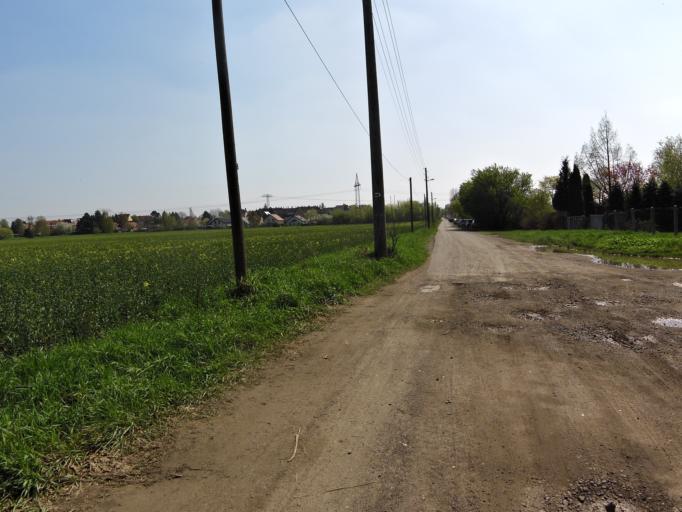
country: DE
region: Saxony
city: Rackwitz
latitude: 51.3950
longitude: 12.3173
